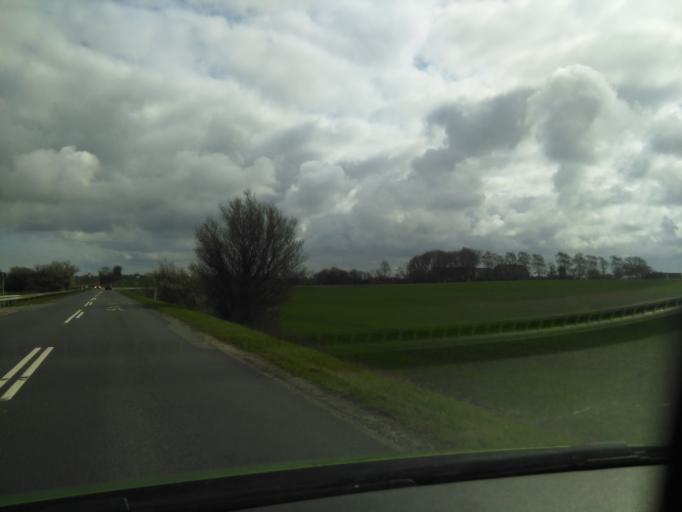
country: DK
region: South Denmark
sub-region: Middelfart Kommune
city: Strib
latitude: 55.5152
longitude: 9.7814
